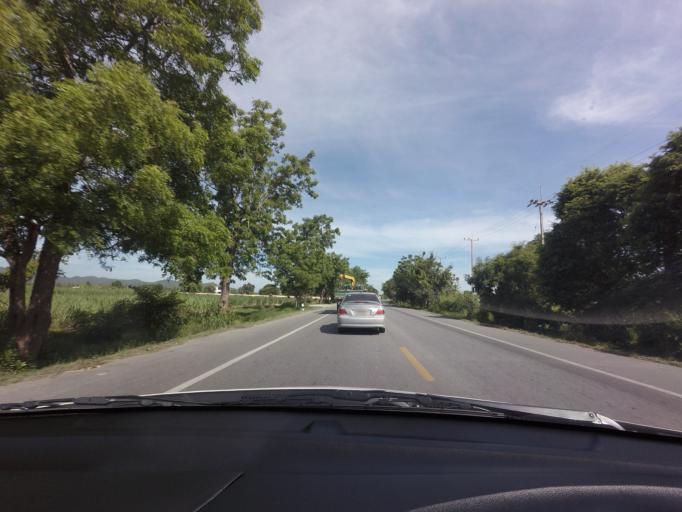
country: TH
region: Kanchanaburi
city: Lao Khwan
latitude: 14.5718
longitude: 99.8767
